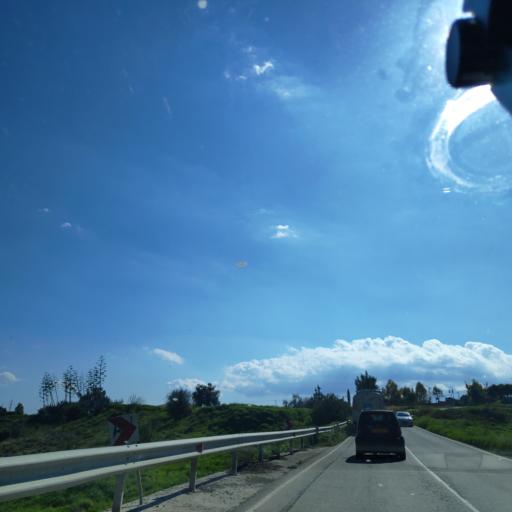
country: CY
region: Lefkosia
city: Tseri
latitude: 35.0260
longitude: 33.3274
